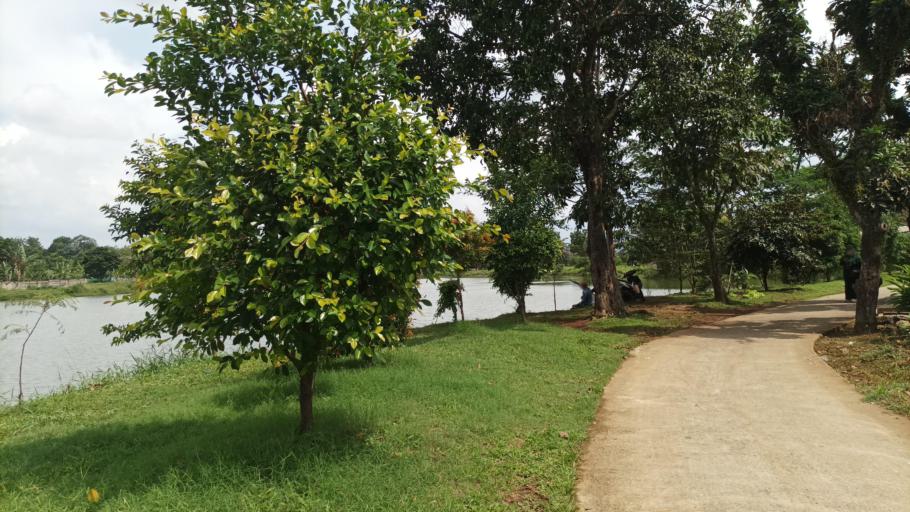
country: ID
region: West Java
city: Cibinong
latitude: -6.4484
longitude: 106.8607
